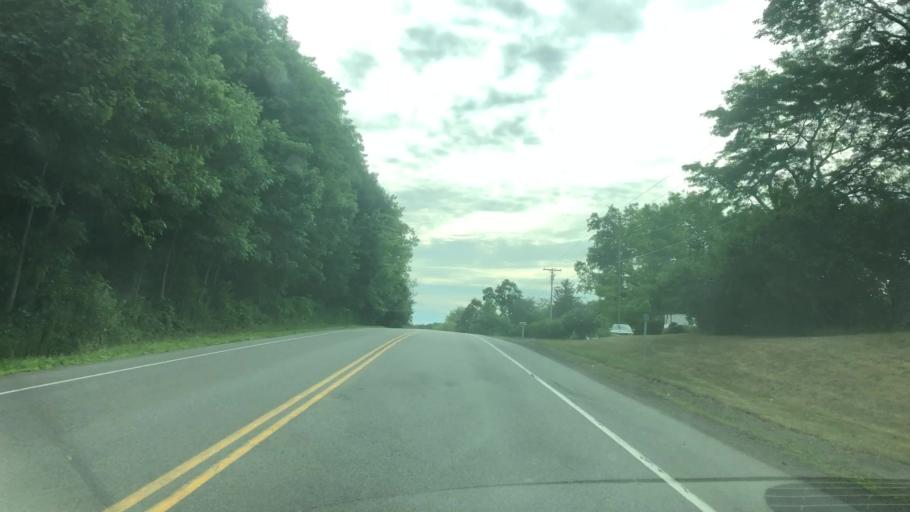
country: US
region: New York
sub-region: Wayne County
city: Macedon
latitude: 43.1349
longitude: -77.3581
